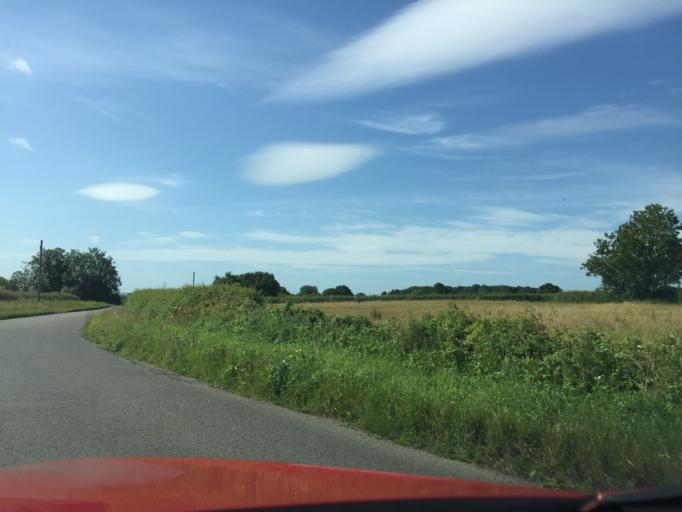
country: GB
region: England
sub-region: Gloucestershire
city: Gloucester
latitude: 51.8281
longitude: -2.3043
